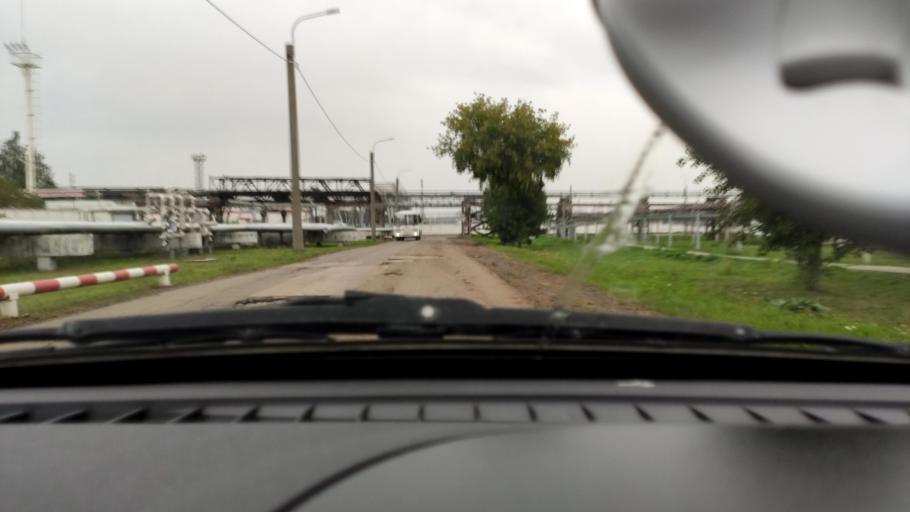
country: RU
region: Perm
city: Gamovo
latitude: 57.9093
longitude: 56.1480
